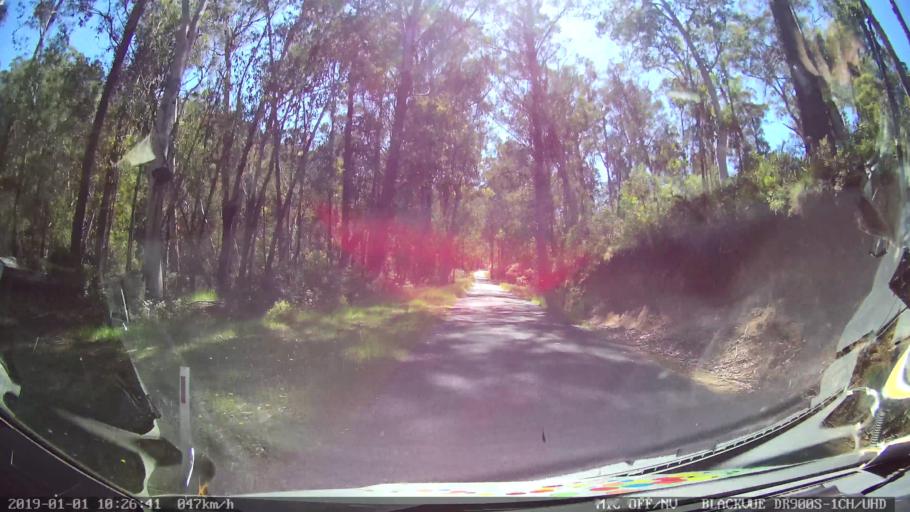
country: AU
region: New South Wales
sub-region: Snowy River
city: Jindabyne
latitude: -36.0669
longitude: 148.2301
